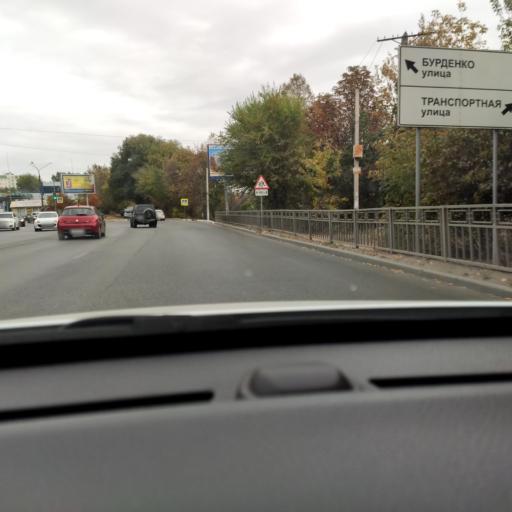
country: RU
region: Voronezj
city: Voronezh
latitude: 51.6925
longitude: 39.2049
